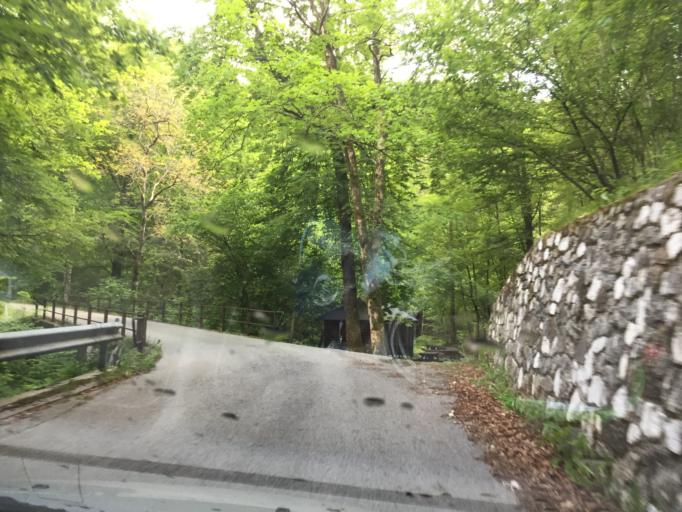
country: IT
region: Friuli Venezia Giulia
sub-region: Provincia di Pordenone
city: Clauzetto
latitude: 46.2772
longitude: 12.9227
